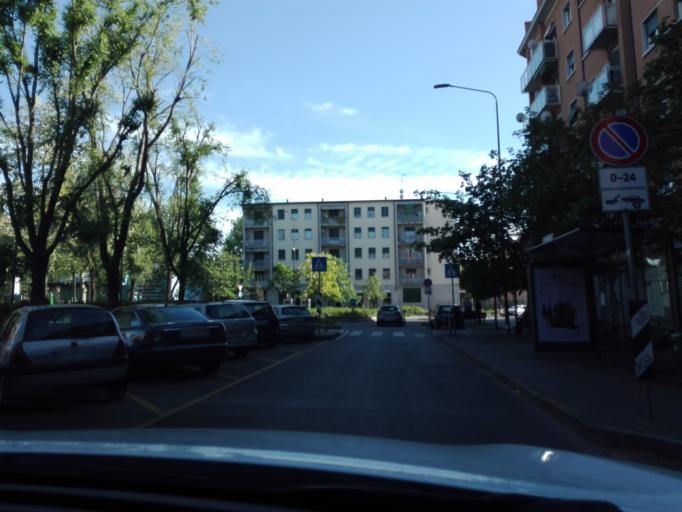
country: IT
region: Lombardy
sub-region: Citta metropolitana di Milano
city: Romano Banco
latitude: 45.4722
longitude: 9.1368
